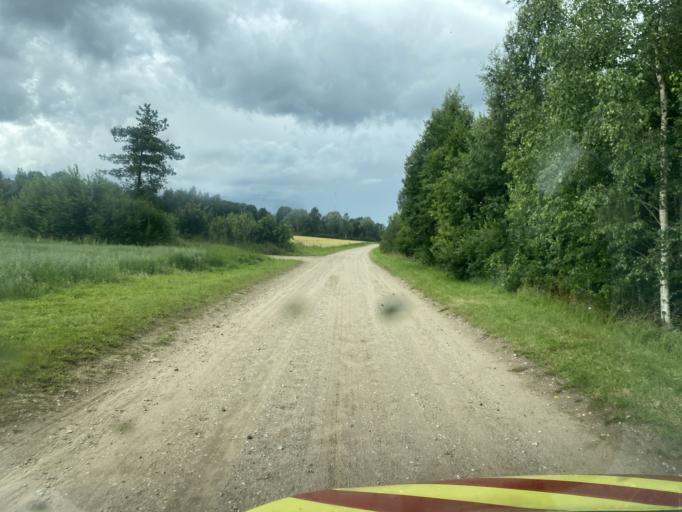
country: EE
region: Valgamaa
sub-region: Torva linn
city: Torva
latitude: 58.0930
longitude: 25.9156
